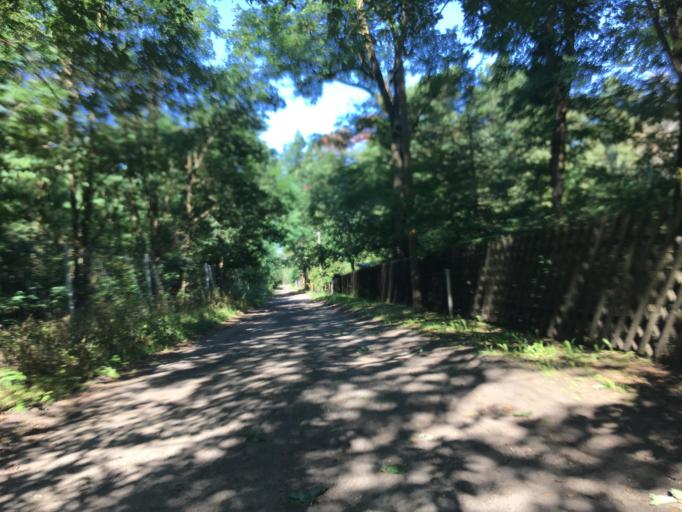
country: DE
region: Brandenburg
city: Gross Koris
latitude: 52.1842
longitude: 13.6522
